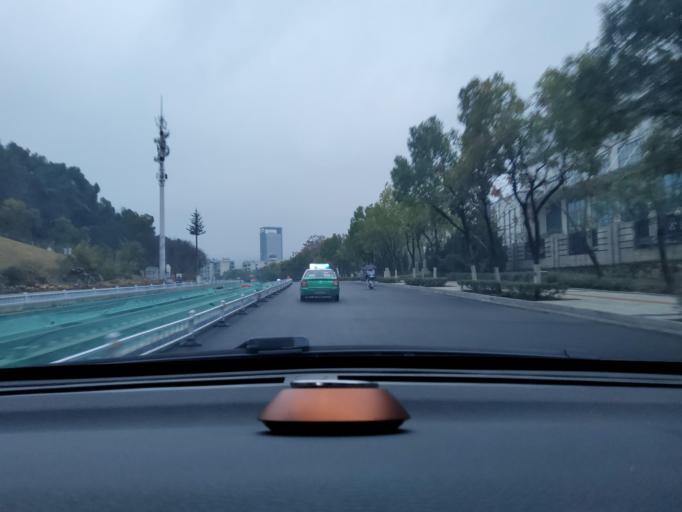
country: CN
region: Hubei
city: Tuanchengshan
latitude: 30.1938
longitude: 115.0234
